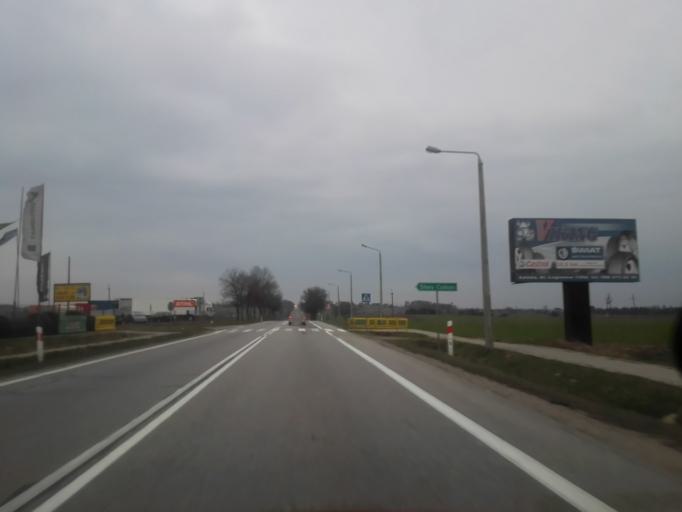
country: PL
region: Podlasie
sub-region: Powiat lomzynski
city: Piatnica
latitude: 53.2434
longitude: 22.1173
